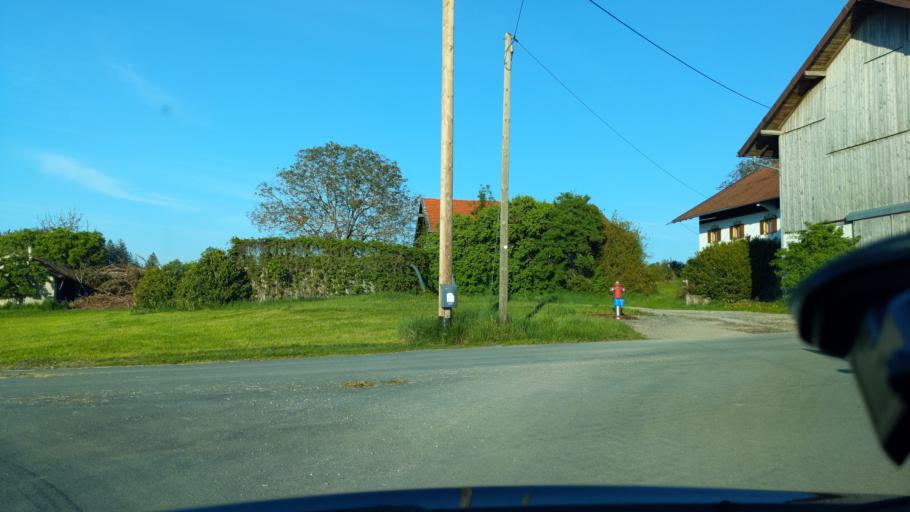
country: DE
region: Bavaria
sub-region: Upper Bavaria
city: Ebersberg
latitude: 48.0707
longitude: 11.9946
